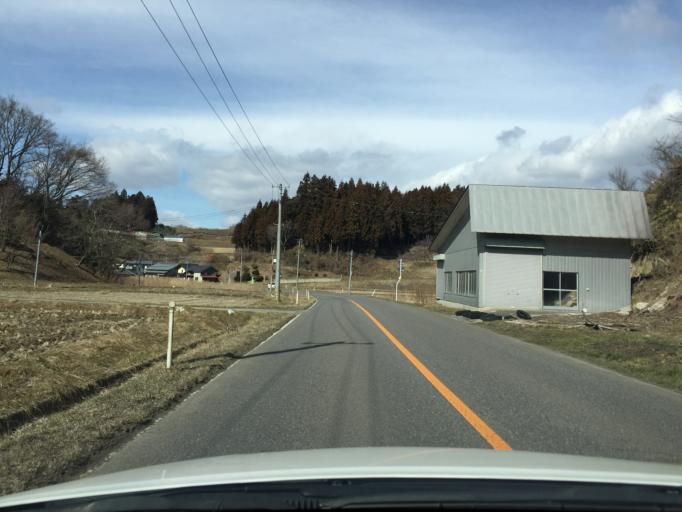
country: JP
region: Fukushima
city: Funehikimachi-funehiki
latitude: 37.4095
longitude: 140.5467
